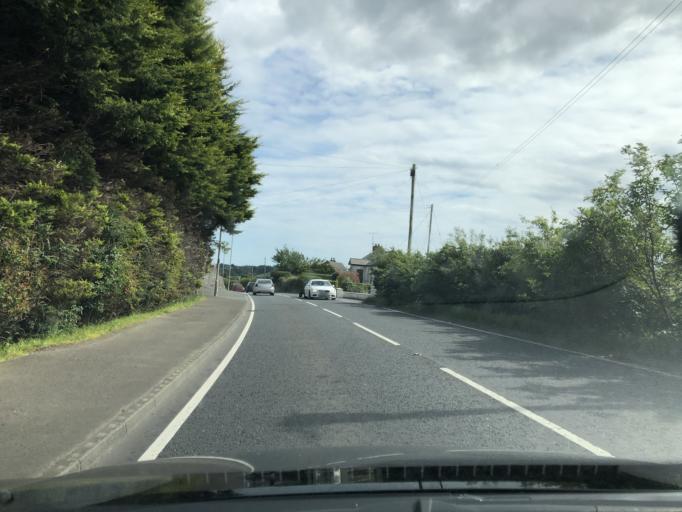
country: GB
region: Northern Ireland
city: Ballynahinch
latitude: 54.3756
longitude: -5.8671
